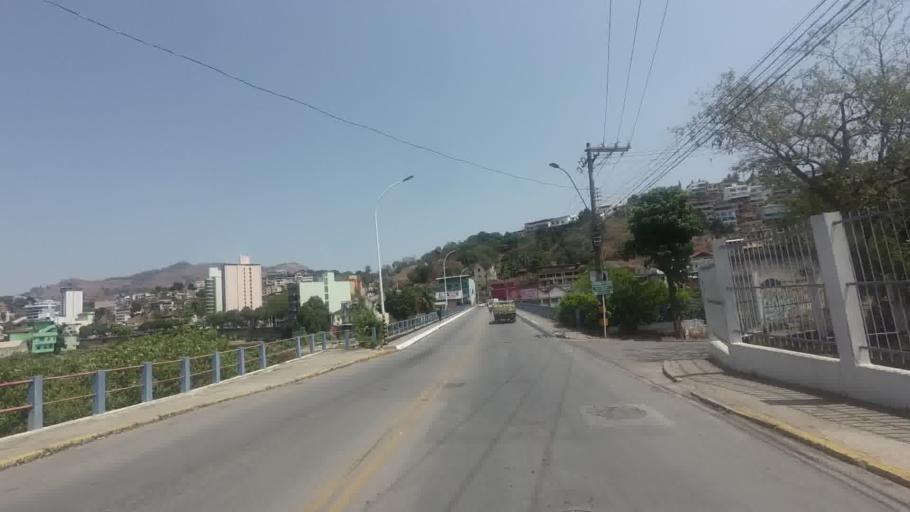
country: BR
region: Espirito Santo
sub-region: Cachoeiro De Itapemirim
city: Cachoeiro de Itapemirim
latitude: -20.8393
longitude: -41.1213
